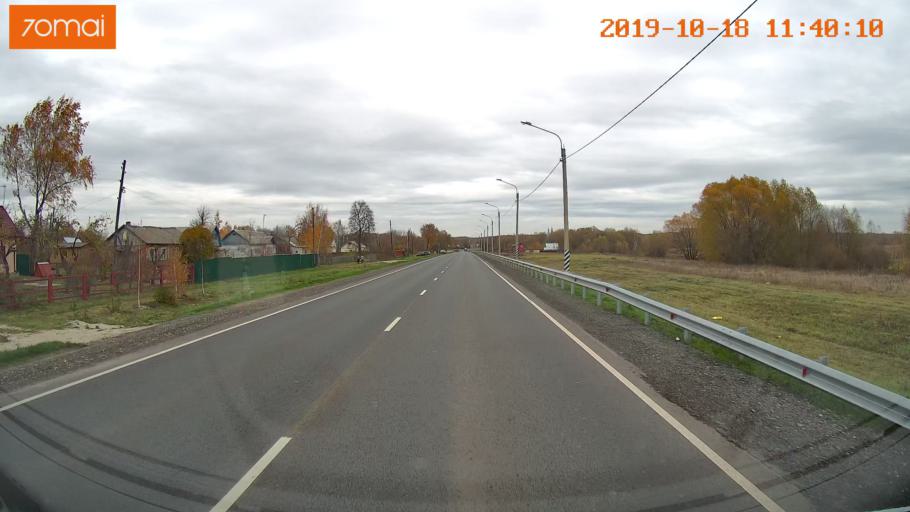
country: RU
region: Rjazan
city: Oktyabr'skiy
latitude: 54.1779
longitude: 38.8866
